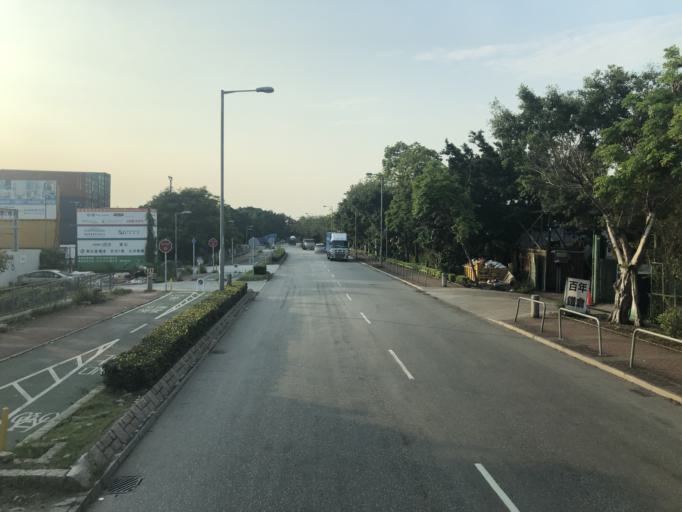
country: HK
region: Yuen Long
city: Yuen Long Kau Hui
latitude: 22.4569
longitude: 113.9916
